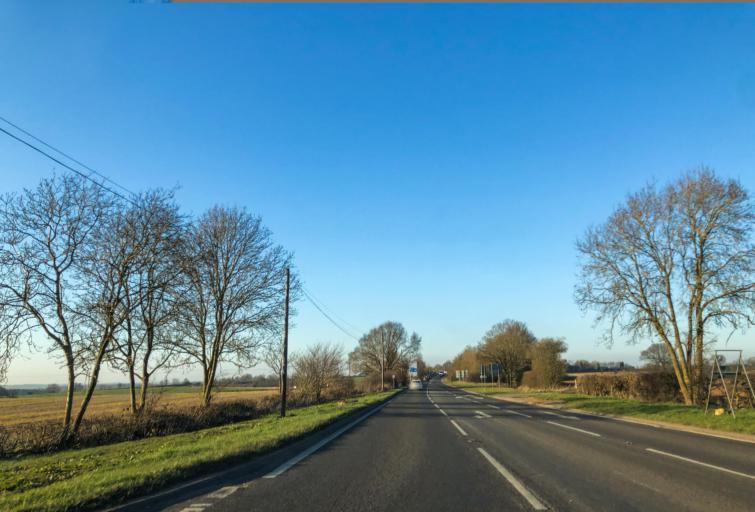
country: GB
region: England
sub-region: Warwickshire
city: Warwick
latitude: 52.2369
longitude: -1.5525
